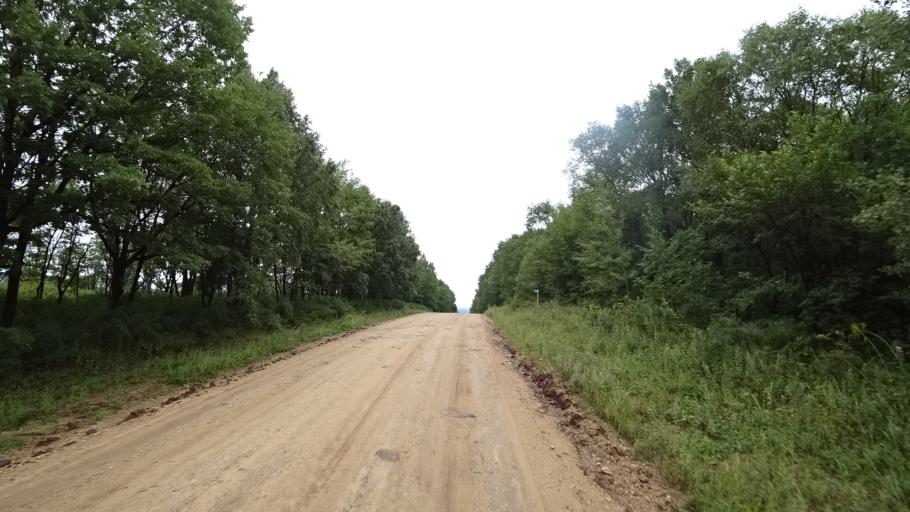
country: RU
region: Primorskiy
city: Ivanovka
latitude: 44.0469
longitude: 132.5453
